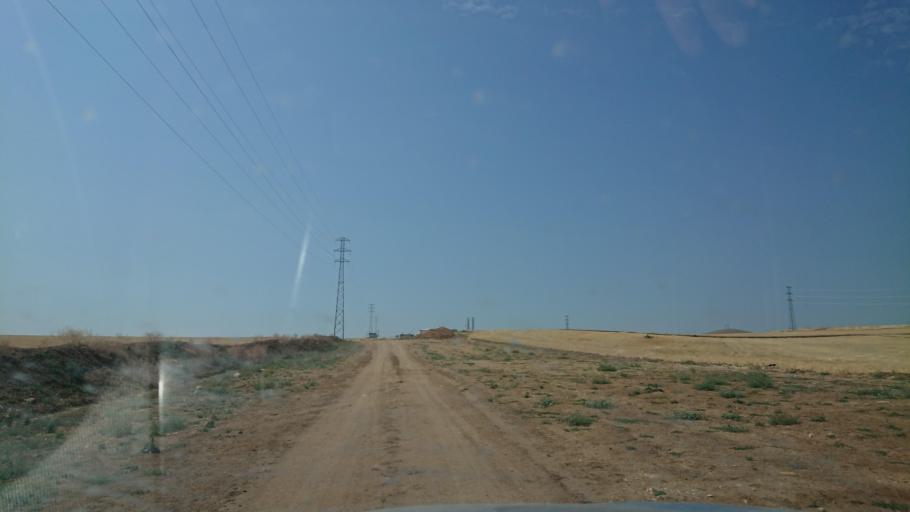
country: TR
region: Aksaray
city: Sariyahsi
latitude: 38.9534
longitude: 33.9132
